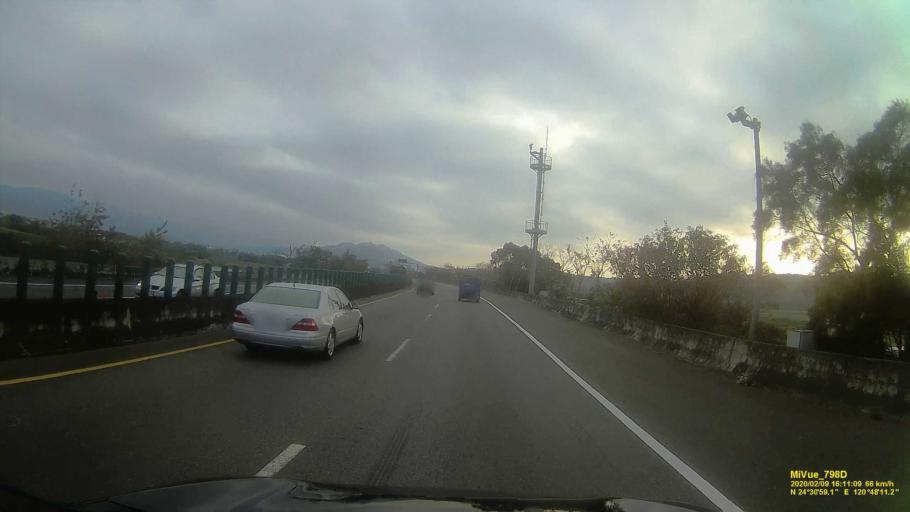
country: TW
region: Taiwan
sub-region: Miaoli
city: Miaoli
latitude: 24.5161
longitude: 120.8030
